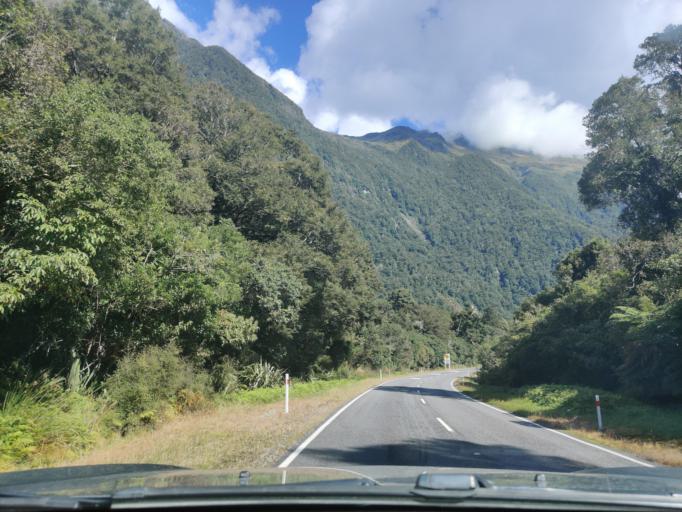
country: NZ
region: Otago
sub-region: Queenstown-Lakes District
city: Wanaka
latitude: -43.9678
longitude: 169.1706
